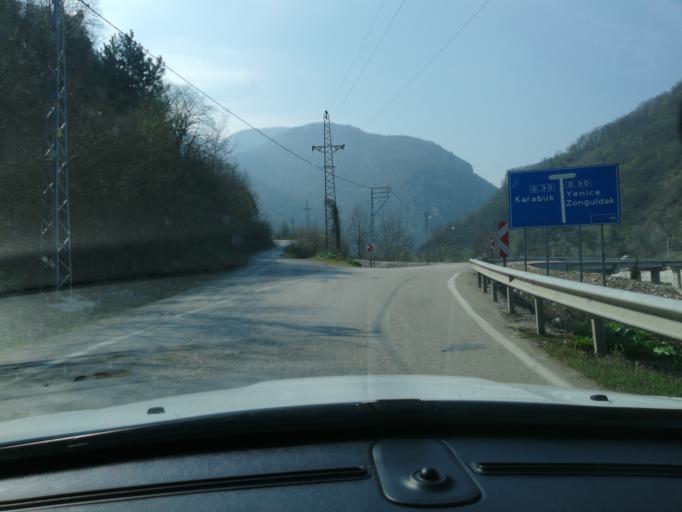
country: TR
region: Karabuk
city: Yenice
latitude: 41.2084
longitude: 32.3674
